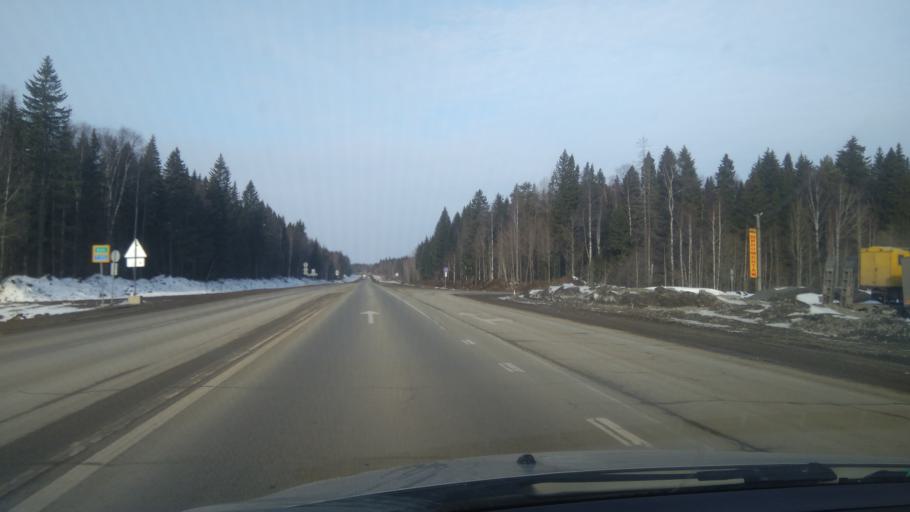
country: RU
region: Sverdlovsk
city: Bisert'
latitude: 56.8270
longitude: 59.1513
